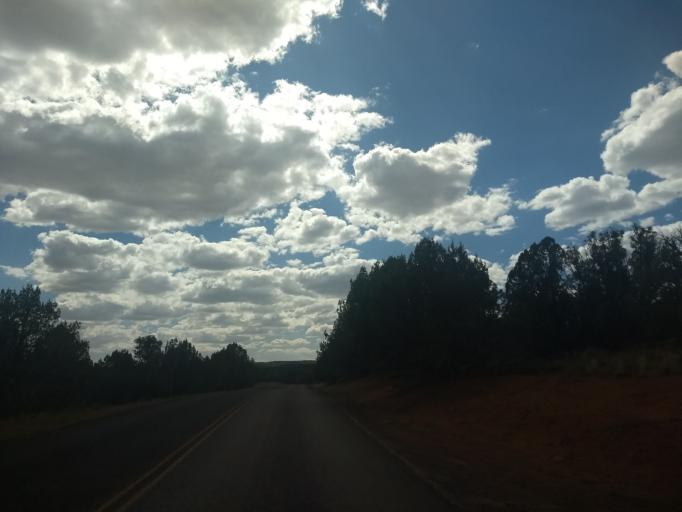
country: US
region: Utah
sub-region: Kane County
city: Kanab
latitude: 37.1465
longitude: -112.5512
